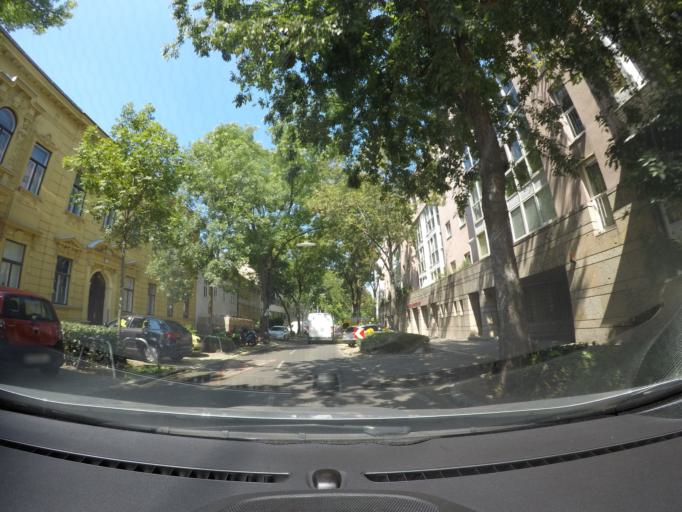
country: AT
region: Lower Austria
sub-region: Politischer Bezirk Modling
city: Perchtoldsdorf
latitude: 48.1917
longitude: 16.2687
